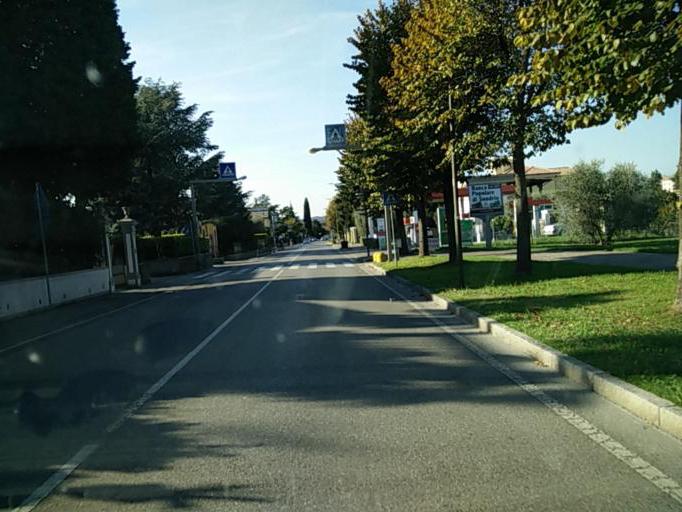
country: IT
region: Lombardy
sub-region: Provincia di Brescia
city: Desenzano del Garda
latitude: 45.4614
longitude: 10.5586
